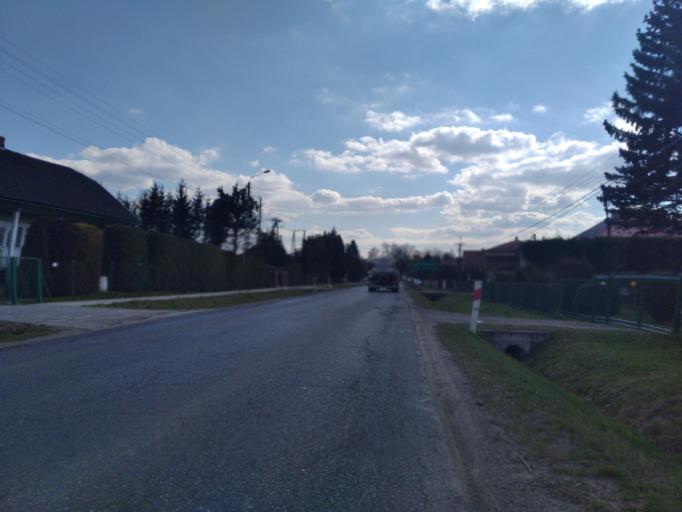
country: PL
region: Subcarpathian Voivodeship
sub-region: Powiat brzozowski
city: Grabownica Starzenska
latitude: 49.6605
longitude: 22.0792
